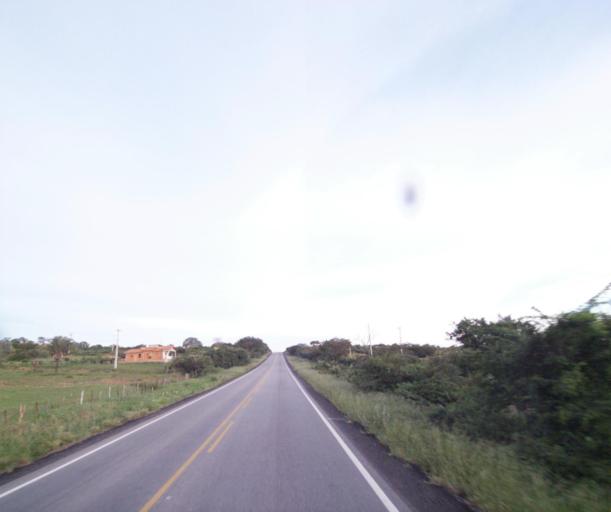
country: BR
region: Bahia
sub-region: Brumado
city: Brumado
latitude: -14.2430
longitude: -41.8728
